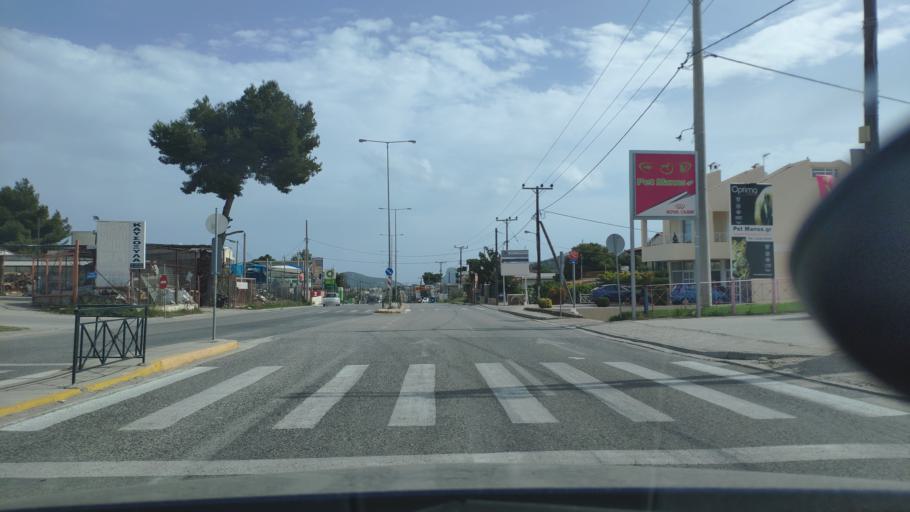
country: GR
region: Attica
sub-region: Nomarchia Anatolikis Attikis
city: Limin Mesoyaias
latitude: 37.8928
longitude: 23.9918
